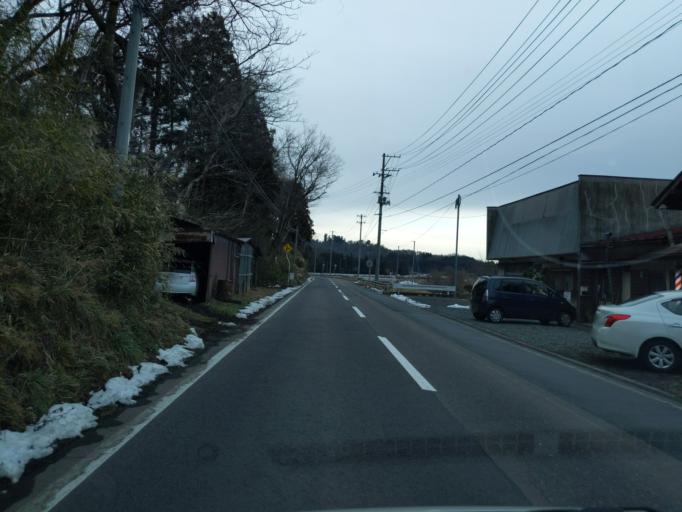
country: JP
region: Iwate
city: Mizusawa
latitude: 39.1643
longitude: 141.1949
